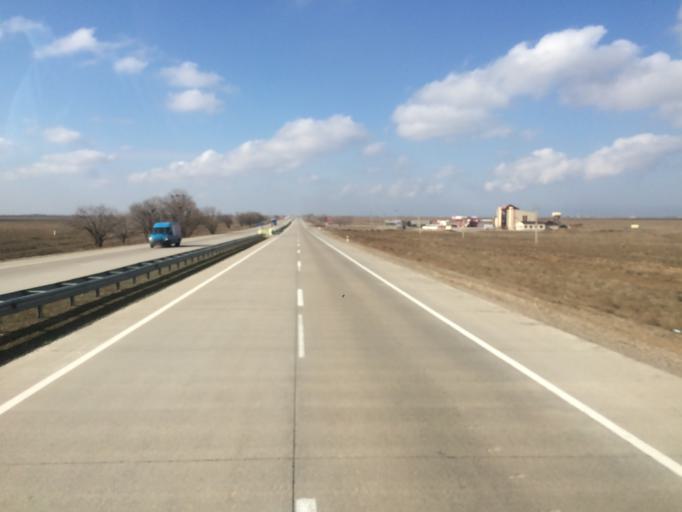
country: KZ
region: Ongtustik Qazaqstan
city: Temirlanovka
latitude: 42.8389
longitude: 69.1100
